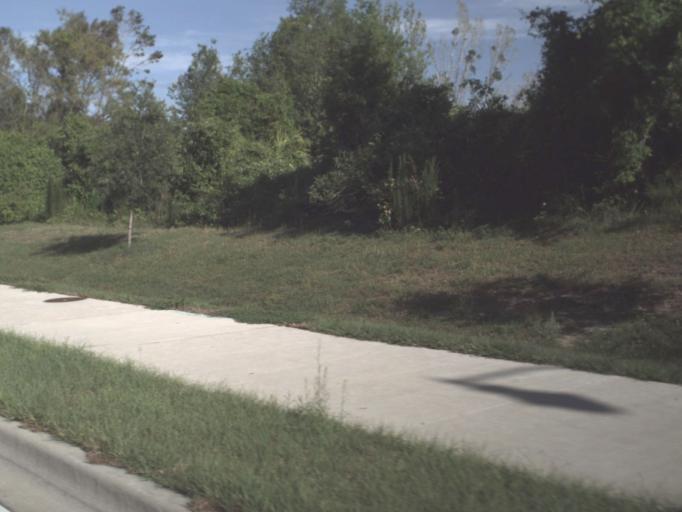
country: US
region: Florida
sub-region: Flagler County
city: Palm Coast
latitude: 29.5551
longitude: -81.2102
